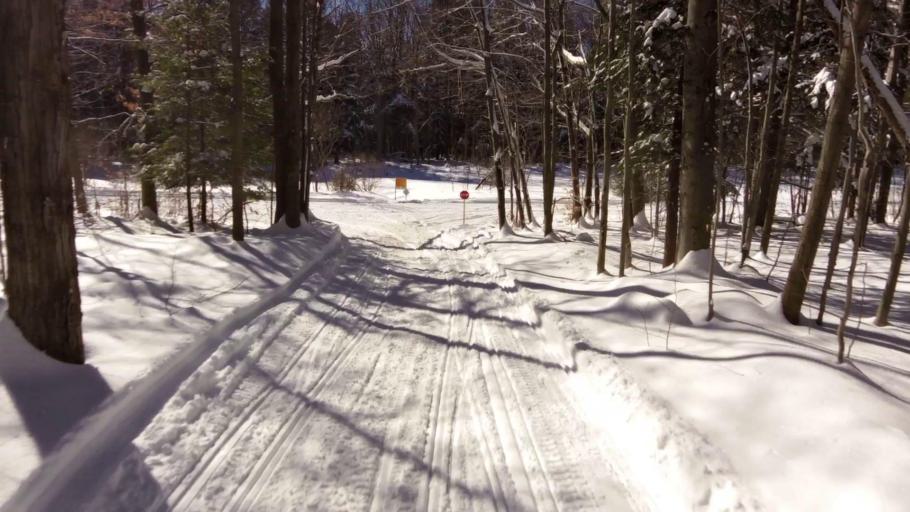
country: US
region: New York
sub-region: Chautauqua County
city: Mayville
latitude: 42.2300
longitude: -79.5229
